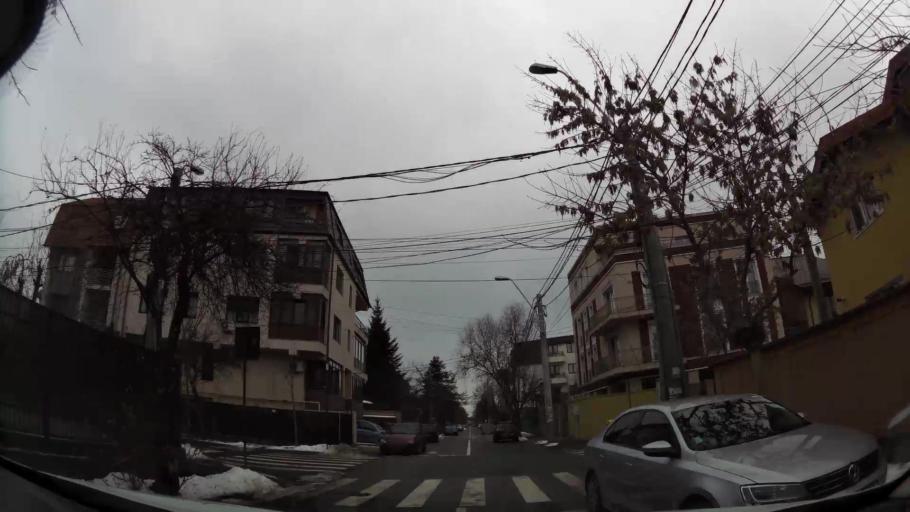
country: RO
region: Ilfov
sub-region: Comuna Chiajna
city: Rosu
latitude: 44.4875
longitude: 26.0301
